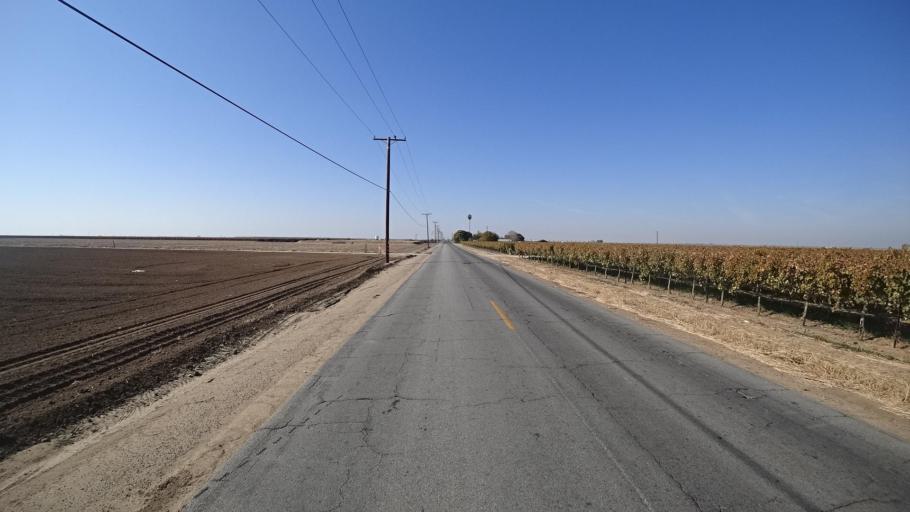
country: US
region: California
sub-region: Kern County
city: McFarland
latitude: 35.7179
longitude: -119.1755
